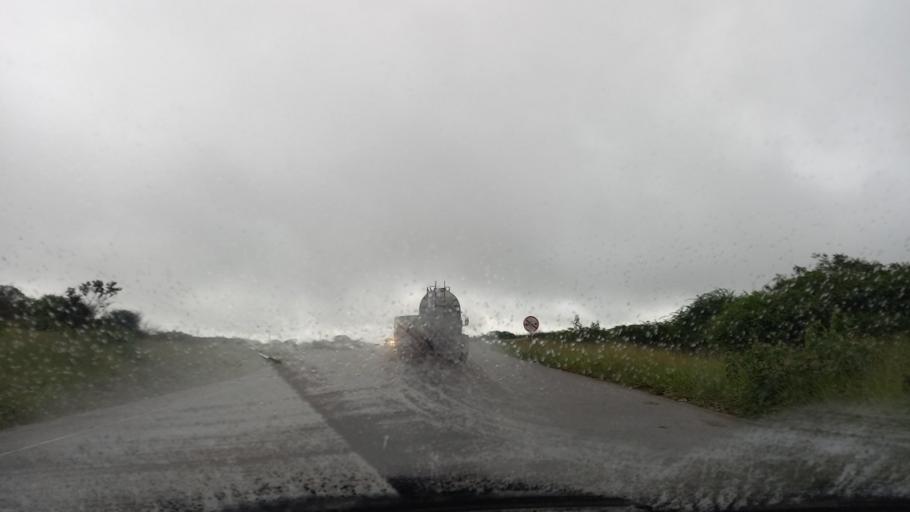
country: BR
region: Pernambuco
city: Garanhuns
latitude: -8.8765
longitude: -36.5072
